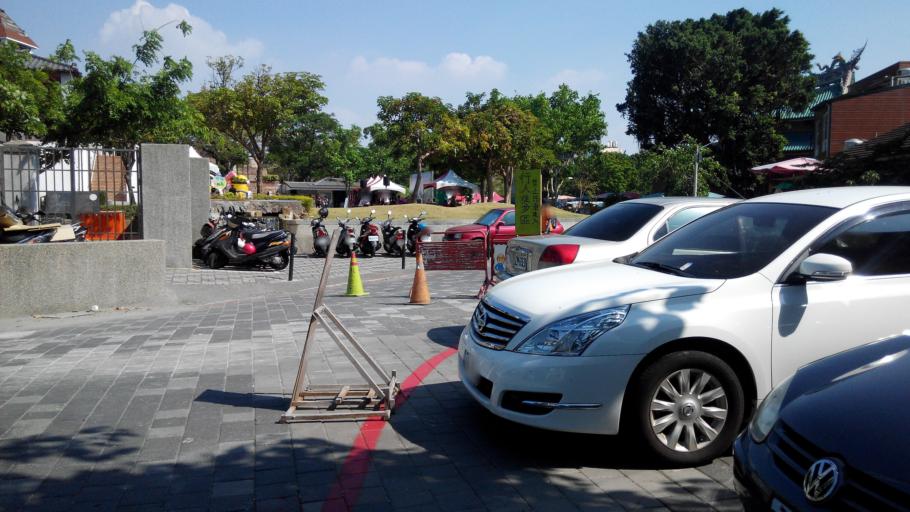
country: TW
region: Taiwan
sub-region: Tainan
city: Tainan
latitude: 23.0009
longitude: 120.1597
